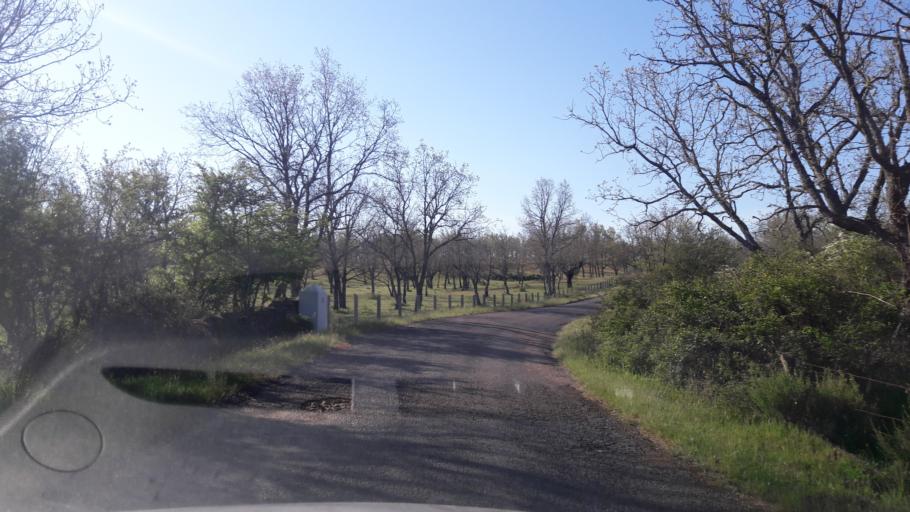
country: ES
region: Castille and Leon
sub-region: Provincia de Salamanca
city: Herguijuela del Campo
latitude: 40.6105
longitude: -5.8462
